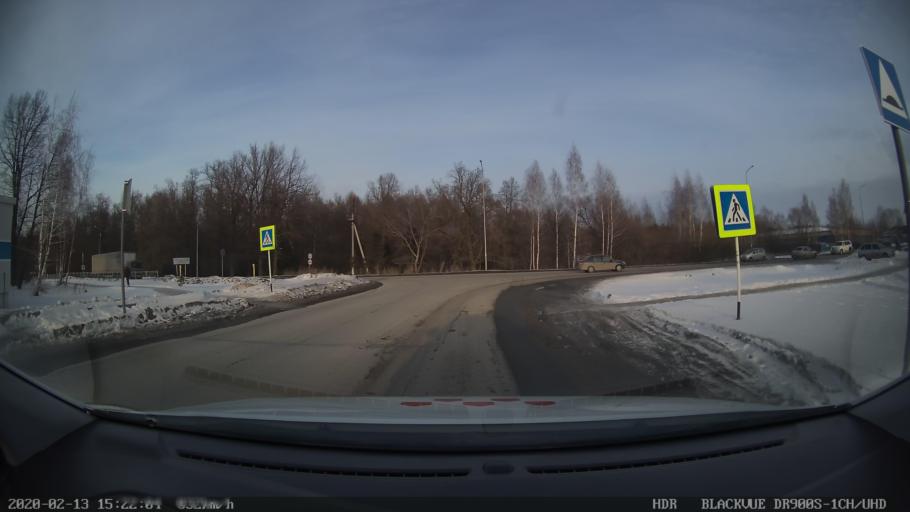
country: RU
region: Tatarstan
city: Vysokaya Gora
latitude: 55.9219
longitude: 49.3058
